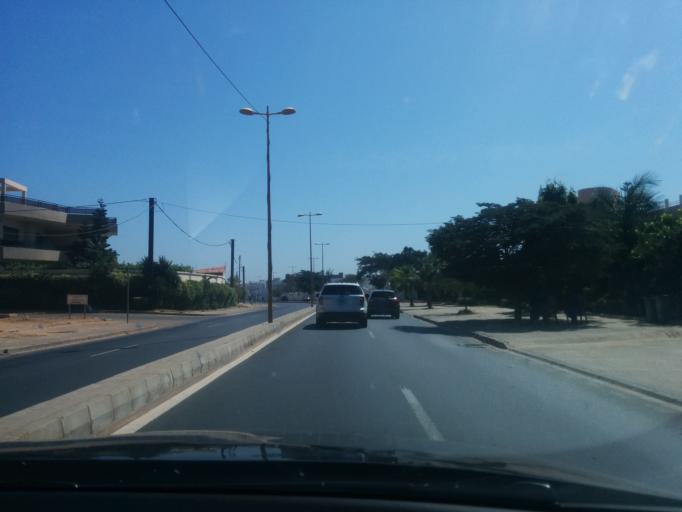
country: SN
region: Dakar
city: Mermoz Boabab
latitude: 14.7027
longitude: -17.4787
